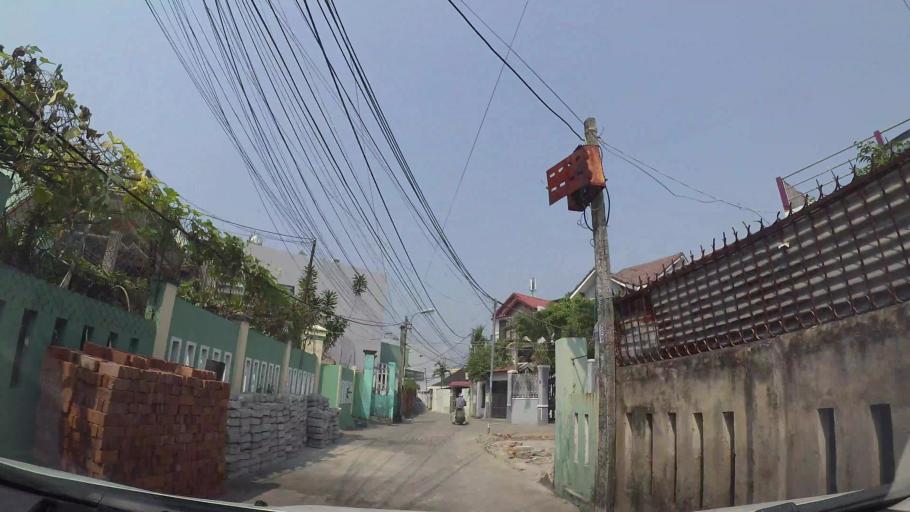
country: VN
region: Da Nang
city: Son Tra
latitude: 16.0431
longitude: 108.2469
